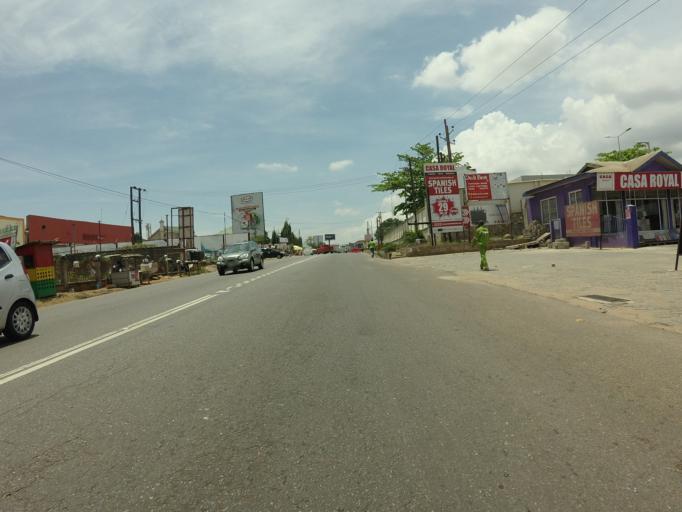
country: GH
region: Greater Accra
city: Medina Estates
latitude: 5.6275
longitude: -0.1510
